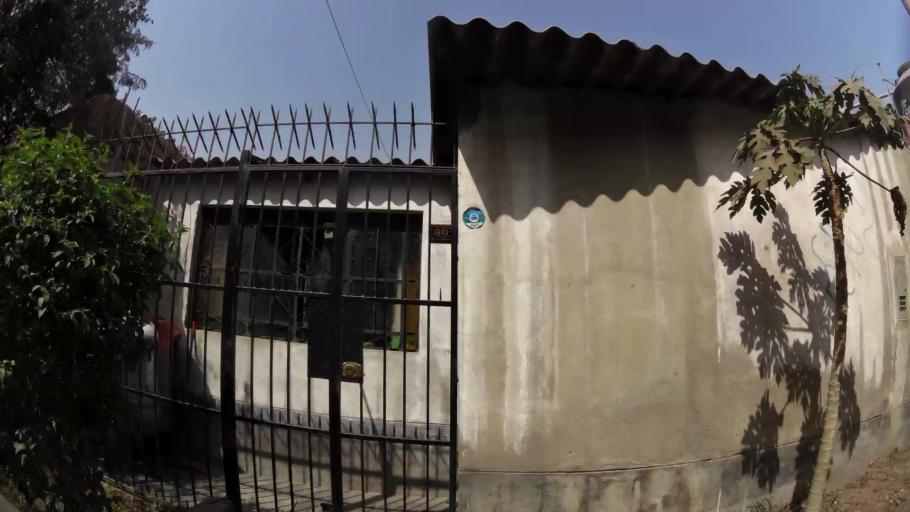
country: PE
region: Lima
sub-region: Lima
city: Asentamiento Humano Nicolas de Pierola
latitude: -11.9374
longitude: -76.7006
